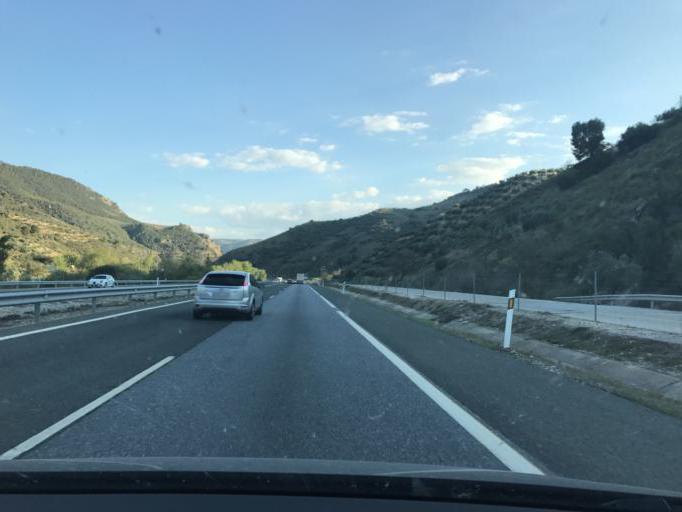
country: ES
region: Andalusia
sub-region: Provincia de Jaen
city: Cambil
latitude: 37.6277
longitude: -3.6035
